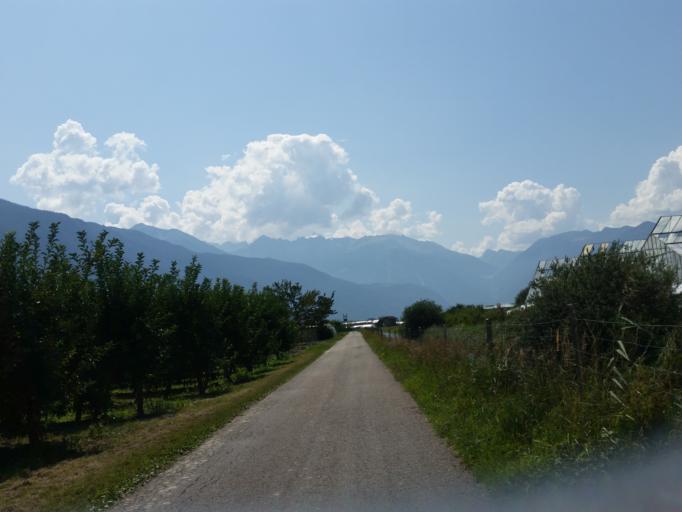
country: CH
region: Valais
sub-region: Martigny District
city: Saillon
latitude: 46.1648
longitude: 7.1684
